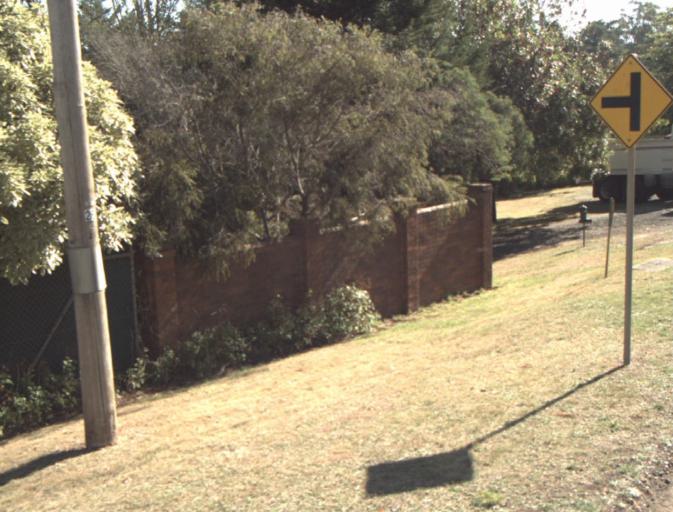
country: AU
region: Tasmania
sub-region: Launceston
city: Mayfield
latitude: -41.3314
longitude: 147.0737
